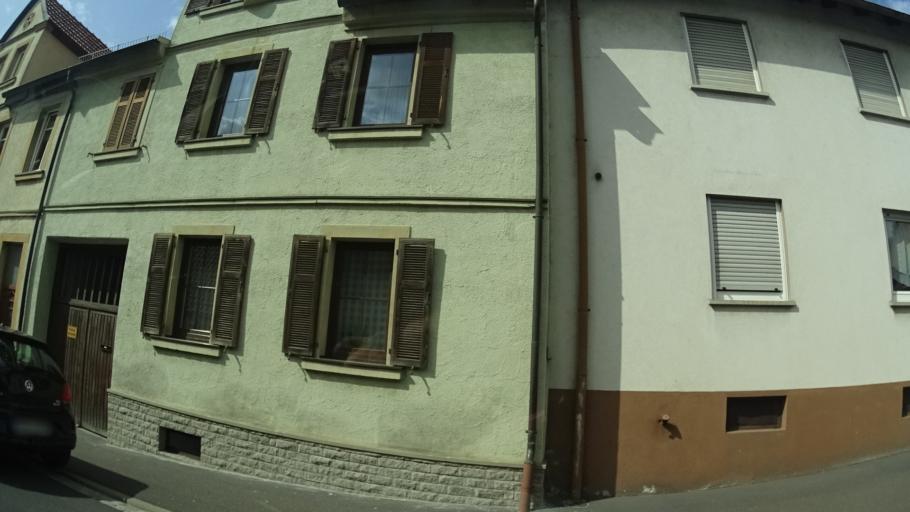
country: DE
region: Bavaria
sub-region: Regierungsbezirk Unterfranken
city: Grettstadt
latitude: 49.9848
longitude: 10.3116
